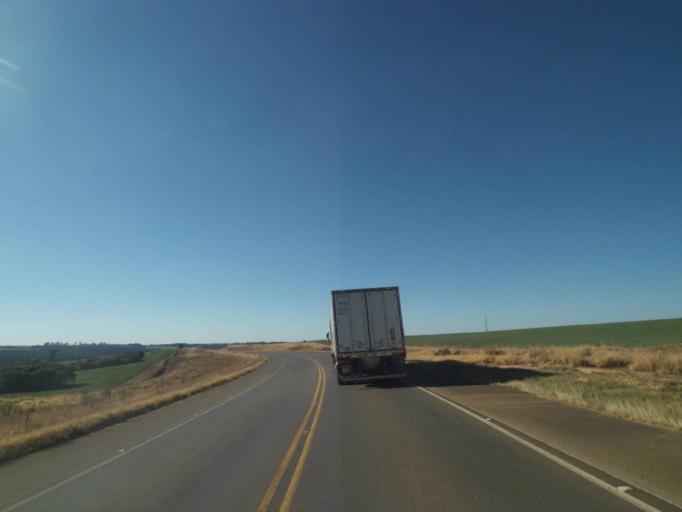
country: BR
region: Parana
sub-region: Tibagi
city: Tibagi
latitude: -24.6280
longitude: -50.4542
